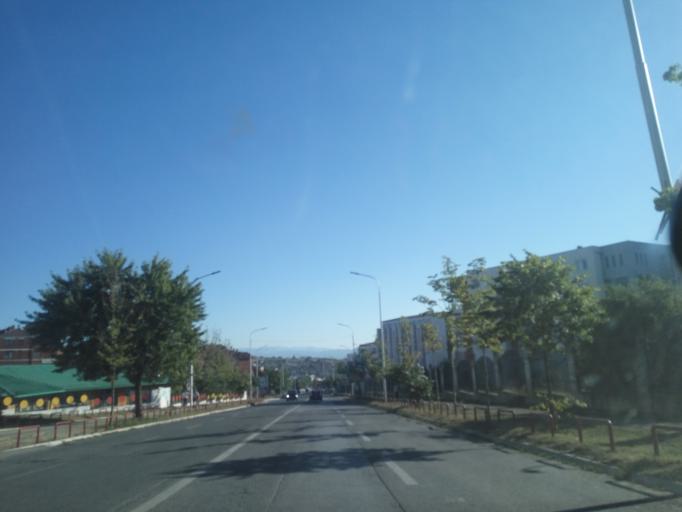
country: XK
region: Pristina
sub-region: Komuna e Prishtines
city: Pristina
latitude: 42.6535
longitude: 21.1672
